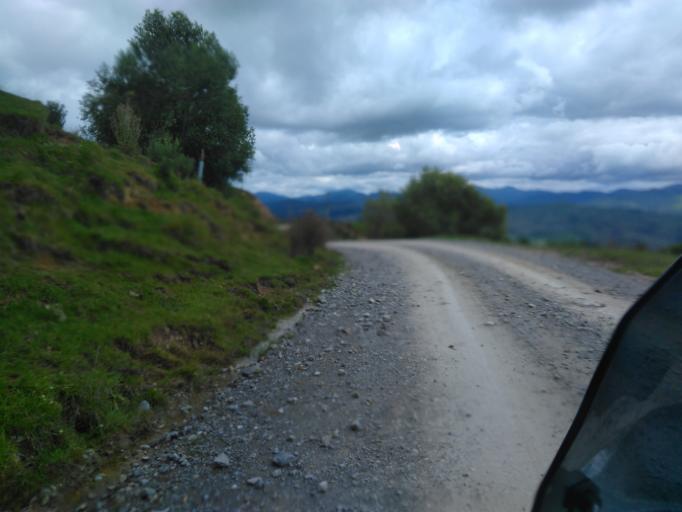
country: NZ
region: Gisborne
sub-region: Gisborne District
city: Gisborne
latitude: -38.0953
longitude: 178.0993
